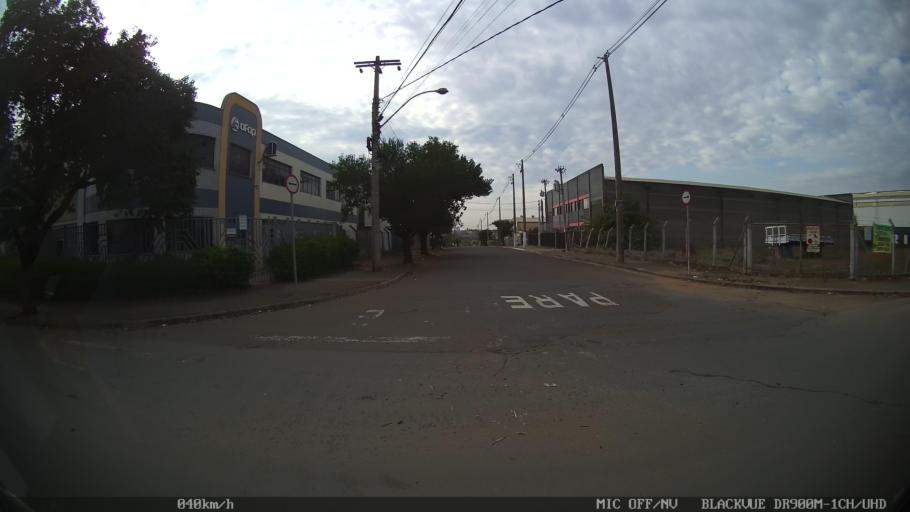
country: BR
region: Sao Paulo
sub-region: Santa Barbara D'Oeste
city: Santa Barbara d'Oeste
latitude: -22.7552
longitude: -47.3863
